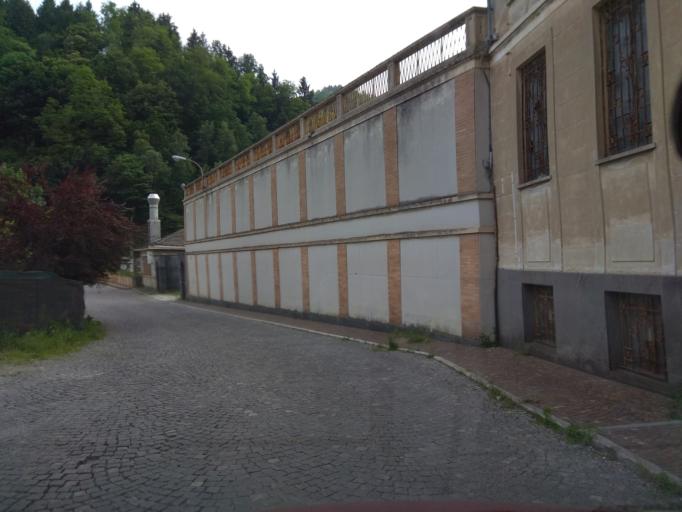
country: IT
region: Piedmont
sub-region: Provincia di Biella
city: Coggiola
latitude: 45.6875
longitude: 8.1763
